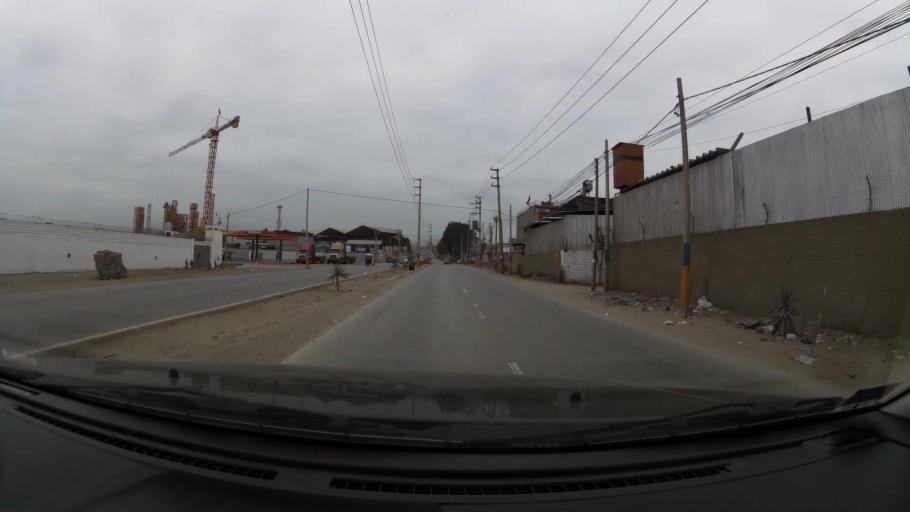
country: PE
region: Lima
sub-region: Lima
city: Surco
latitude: -12.2129
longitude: -76.9650
